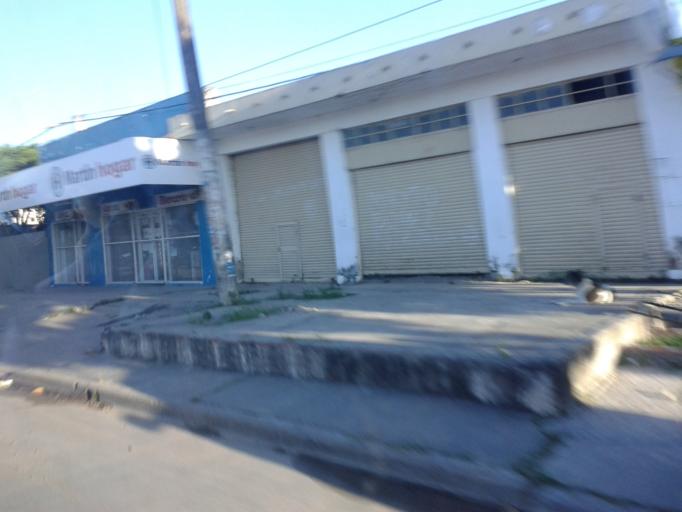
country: AR
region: Formosa
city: Formosa
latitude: -26.1726
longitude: -58.1948
